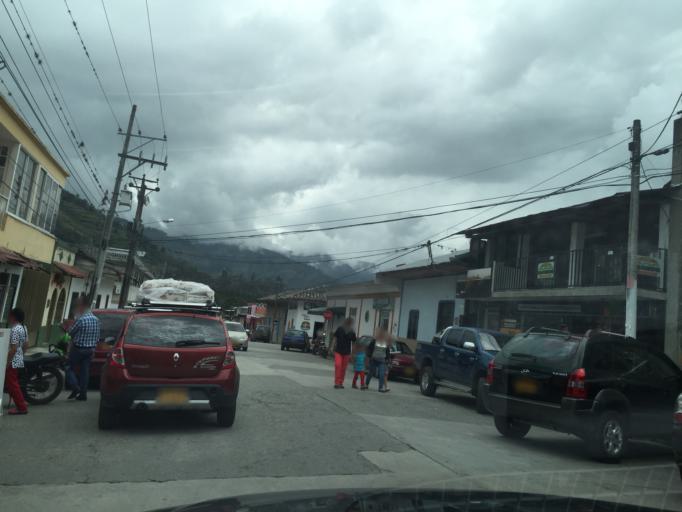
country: CO
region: Tolima
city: Cajamarca
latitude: 4.4407
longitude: -75.4265
